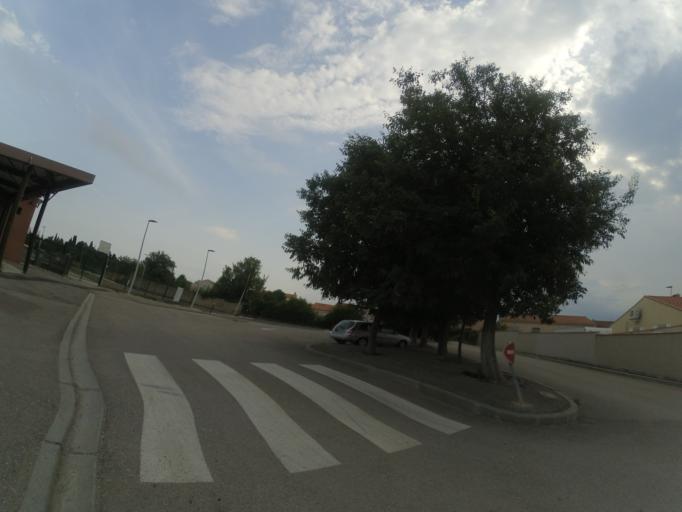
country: FR
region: Languedoc-Roussillon
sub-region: Departement des Pyrenees-Orientales
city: Corneilla-la-Riviere
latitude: 42.6846
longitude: 2.7239
